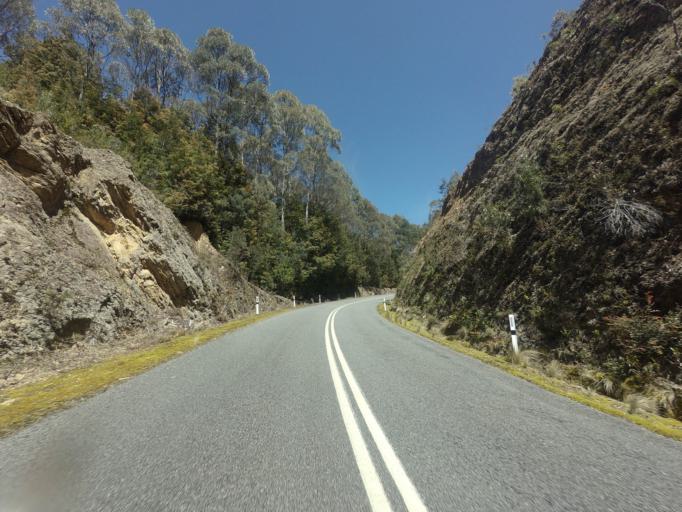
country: AU
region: Tasmania
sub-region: Huon Valley
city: Geeveston
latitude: -42.8162
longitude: 146.3674
